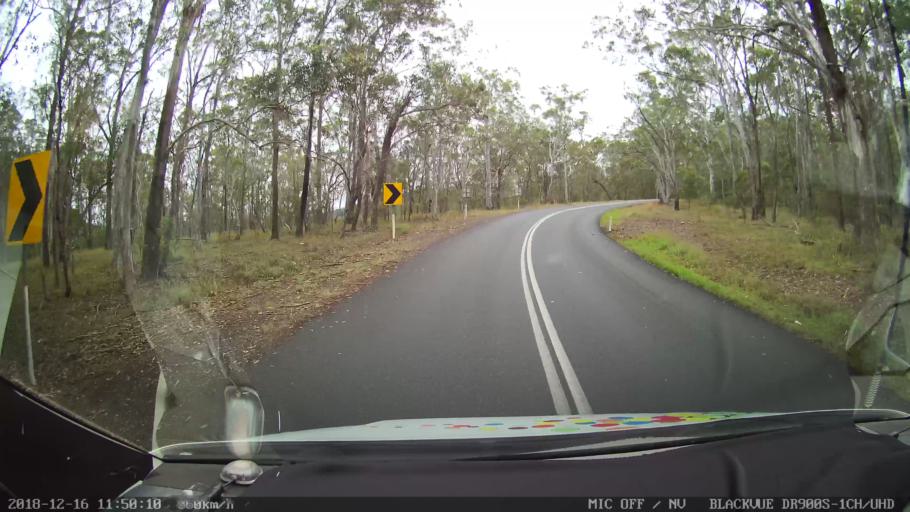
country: AU
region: New South Wales
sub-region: Tenterfield Municipality
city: Carrolls Creek
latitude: -28.9087
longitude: 152.2580
